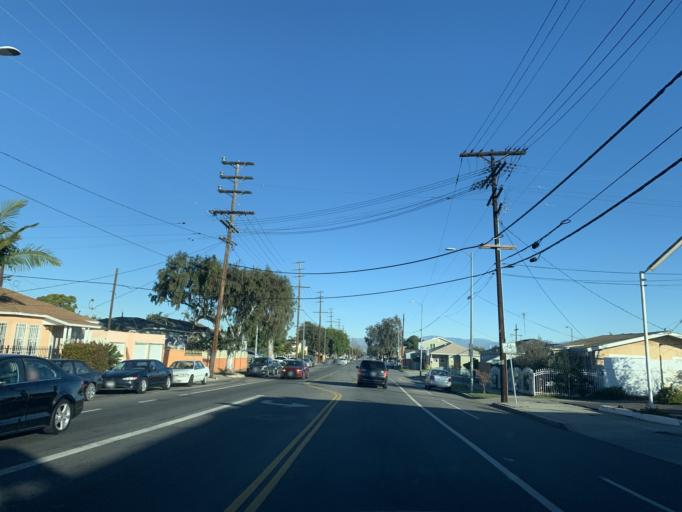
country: US
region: California
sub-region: Los Angeles County
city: West Athens
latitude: 33.9312
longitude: -118.2869
